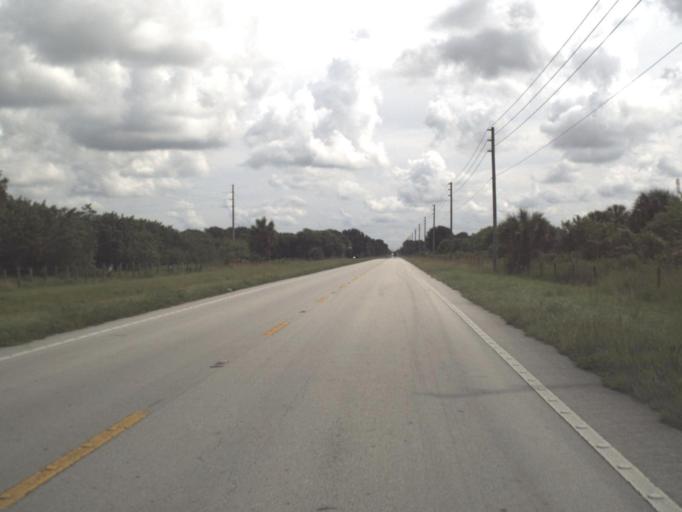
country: US
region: Florida
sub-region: Okeechobee County
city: Okeechobee
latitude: 27.2435
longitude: -80.8731
